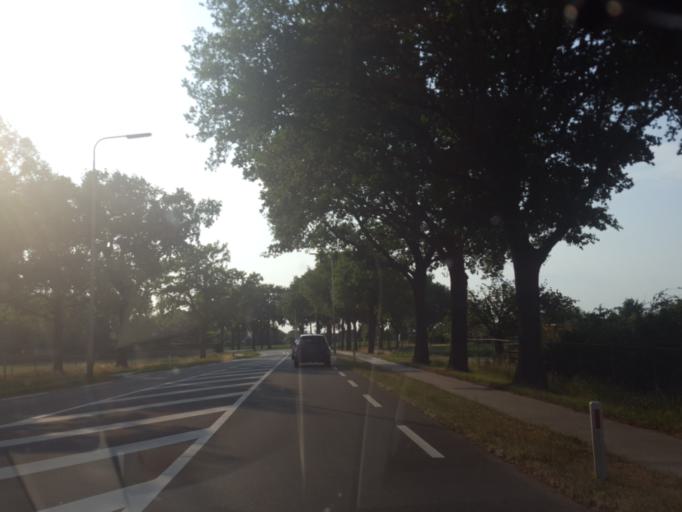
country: NL
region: Limburg
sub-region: Gemeente Leudal
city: Kelpen-Oler
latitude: 51.2364
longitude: 5.7820
